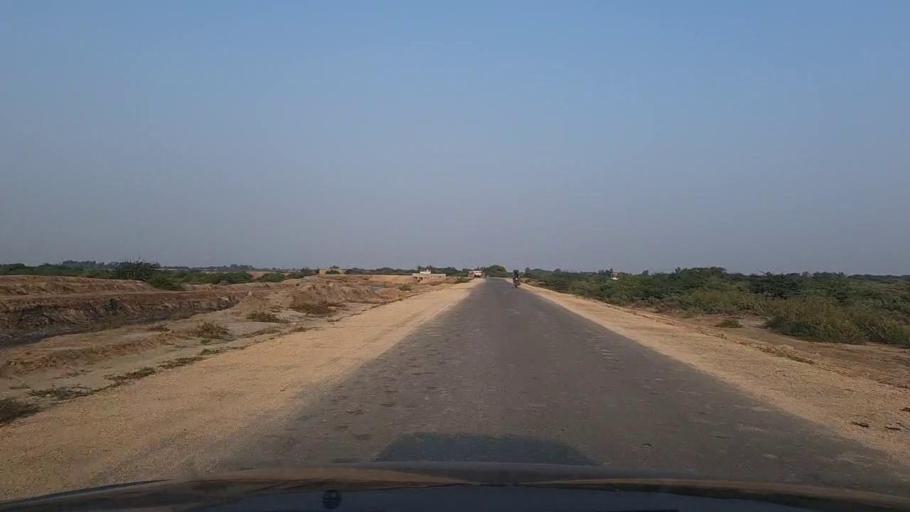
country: PK
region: Sindh
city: Mirpur Sakro
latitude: 24.4451
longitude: 67.7869
